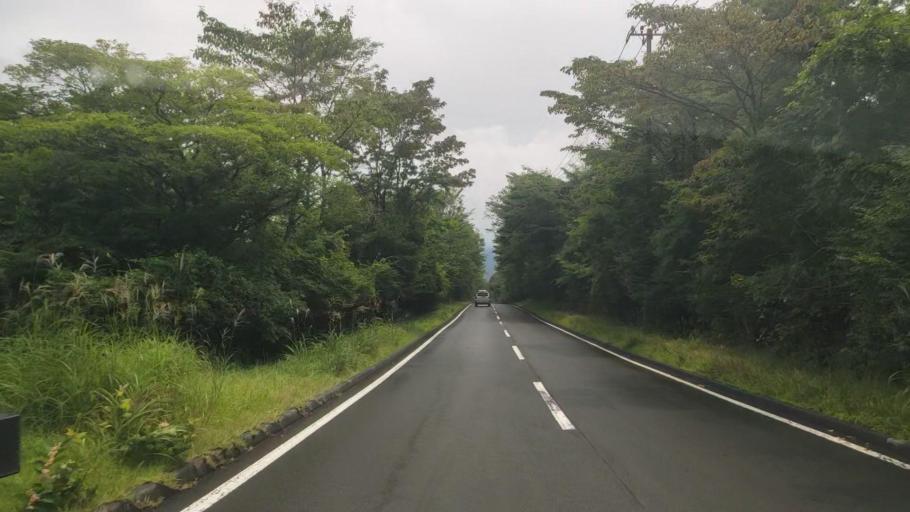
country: JP
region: Shizuoka
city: Gotemba
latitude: 35.2756
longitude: 138.7961
